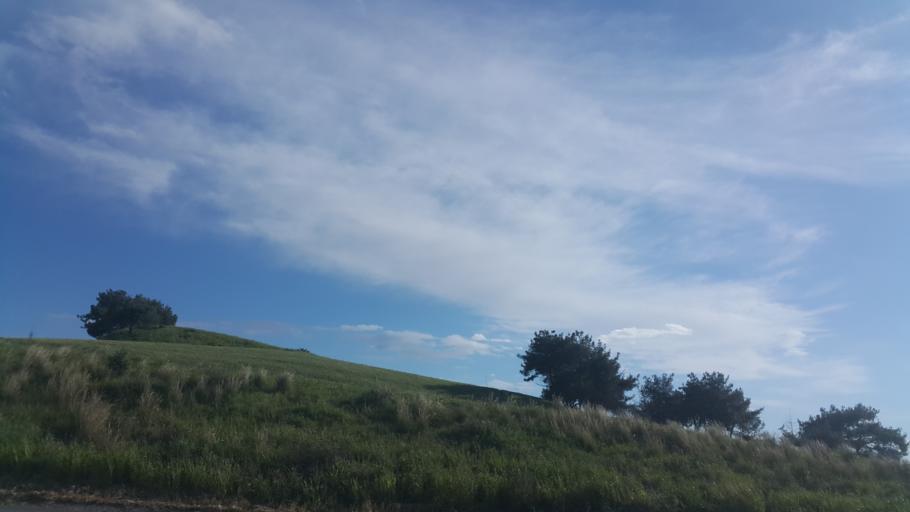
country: TR
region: Adana
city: Yakapinar
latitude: 36.9961
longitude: 35.5723
